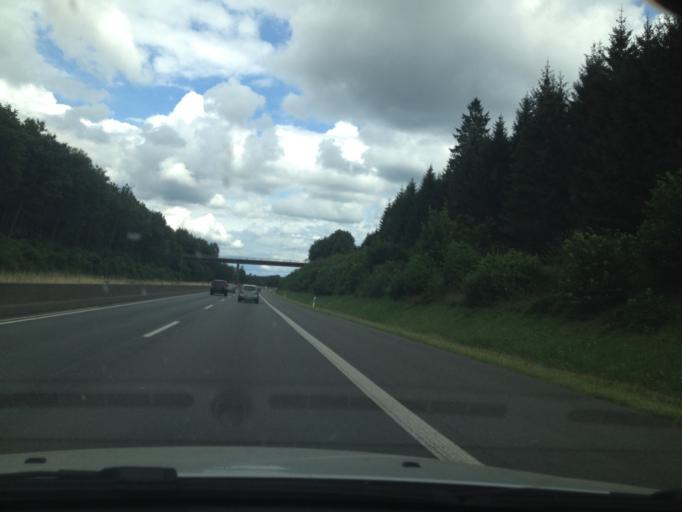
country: DE
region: North Rhine-Westphalia
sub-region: Regierungsbezirk Arnsberg
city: Drolshagen
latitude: 50.9787
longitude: 7.7681
